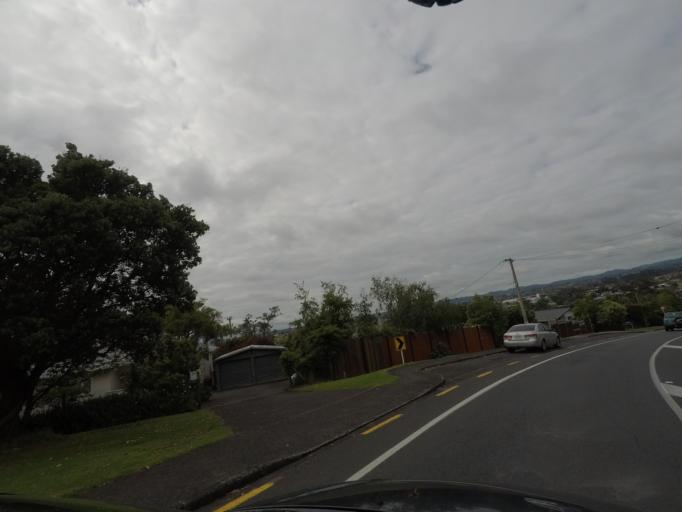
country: NZ
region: Auckland
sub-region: Auckland
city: Rosebank
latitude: -36.8546
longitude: 174.6121
